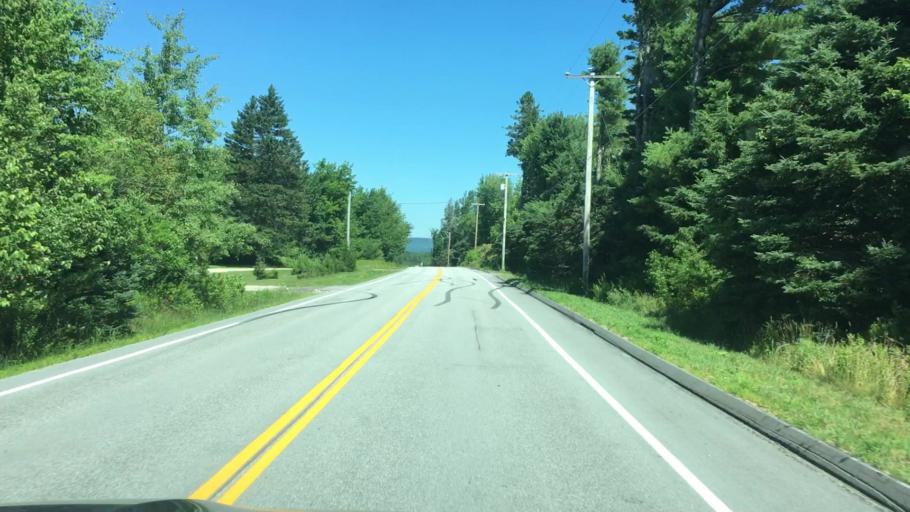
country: US
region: Maine
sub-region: Hancock County
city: Orland
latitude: 44.5337
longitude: -68.6772
